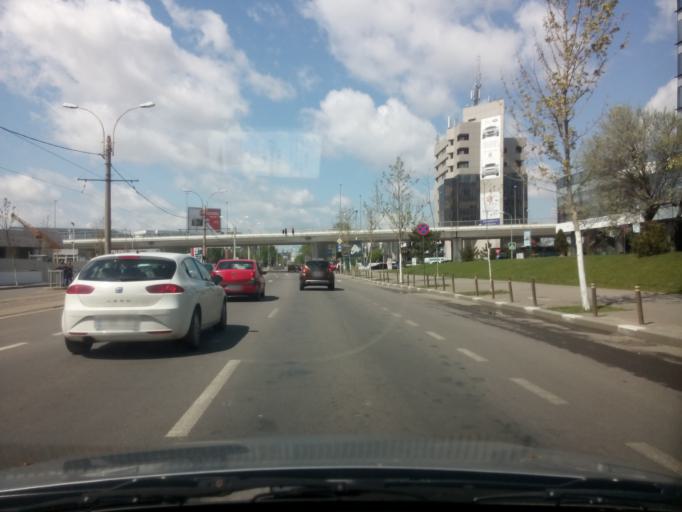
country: RO
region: Bucuresti
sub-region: Municipiul Bucuresti
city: Bucharest
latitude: 44.4795
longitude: 26.1038
